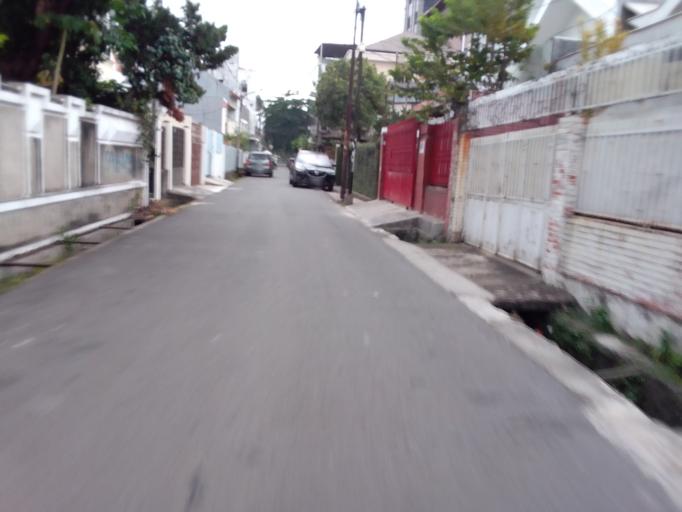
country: ID
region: Jakarta Raya
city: Jakarta
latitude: -6.1747
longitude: 106.8131
